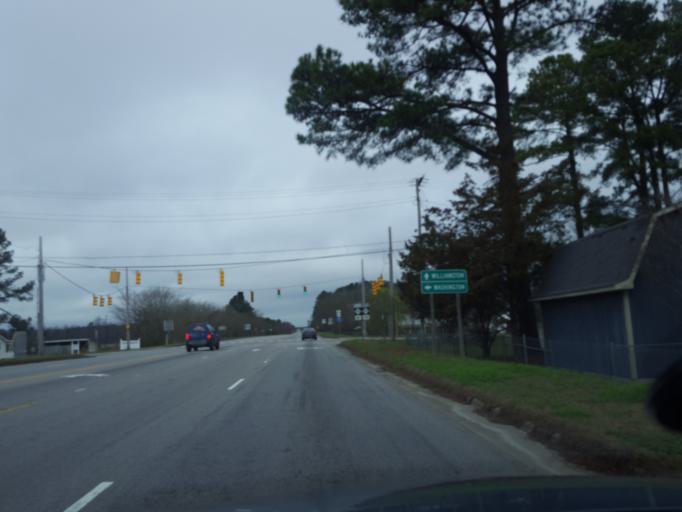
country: US
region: North Carolina
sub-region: Washington County
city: Plymouth
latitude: 35.8062
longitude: -76.8982
